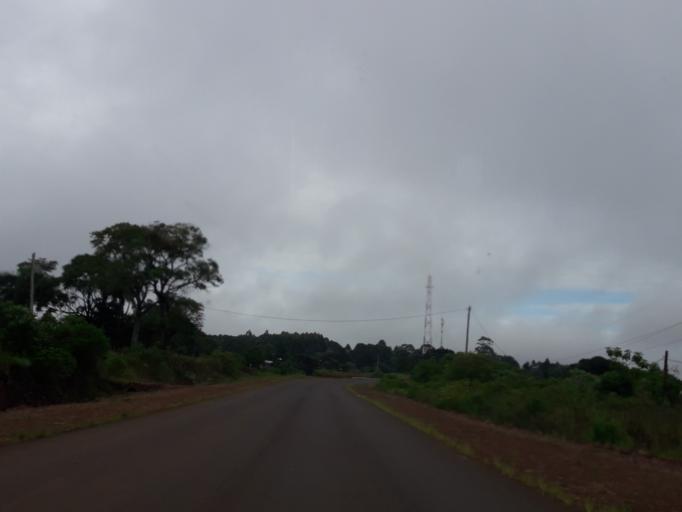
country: AR
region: Misiones
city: Bernardo de Irigoyen
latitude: -26.4230
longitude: -53.8391
